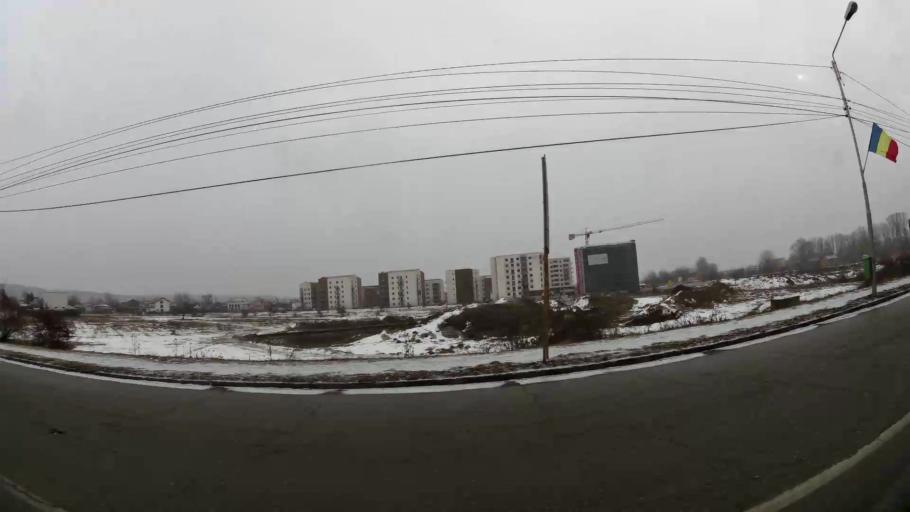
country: RO
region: Dambovita
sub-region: Municipiul Targoviste
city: Targoviste
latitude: 44.9399
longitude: 25.4576
